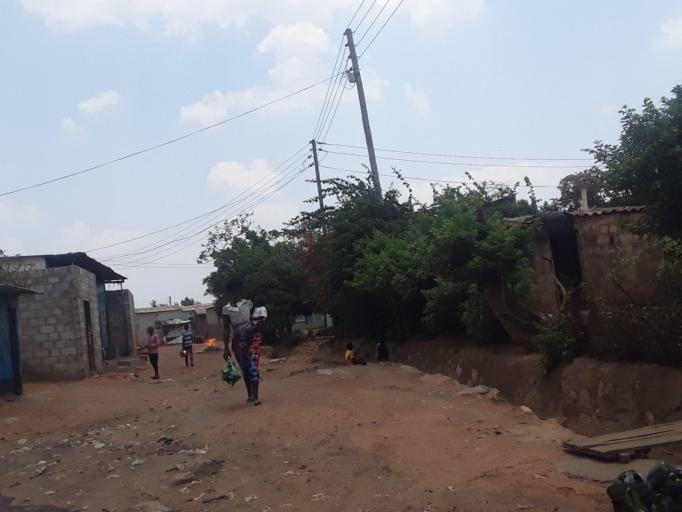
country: ZM
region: Lusaka
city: Lusaka
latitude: -15.3647
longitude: 28.3016
